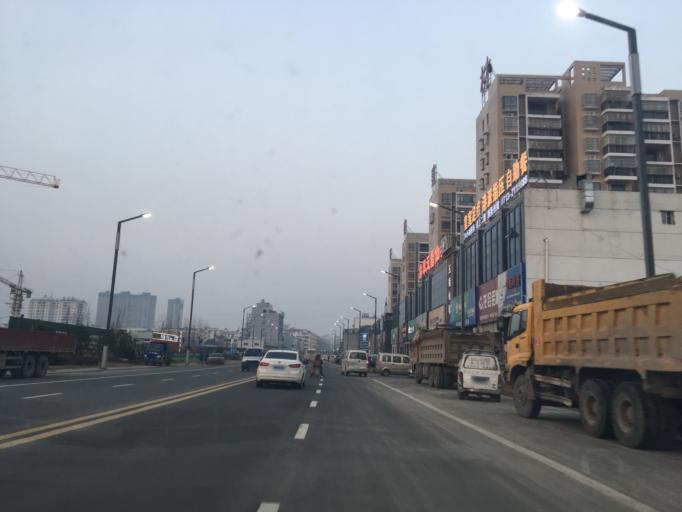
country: CN
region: Hubei
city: Gulou
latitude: 31.1658
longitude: 115.0290
